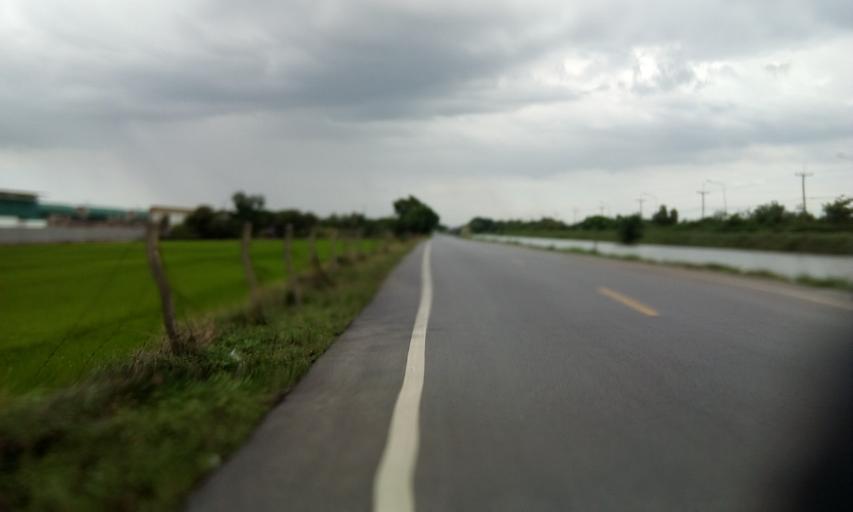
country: TH
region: Pathum Thani
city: Nong Suea
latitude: 14.0676
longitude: 100.8468
